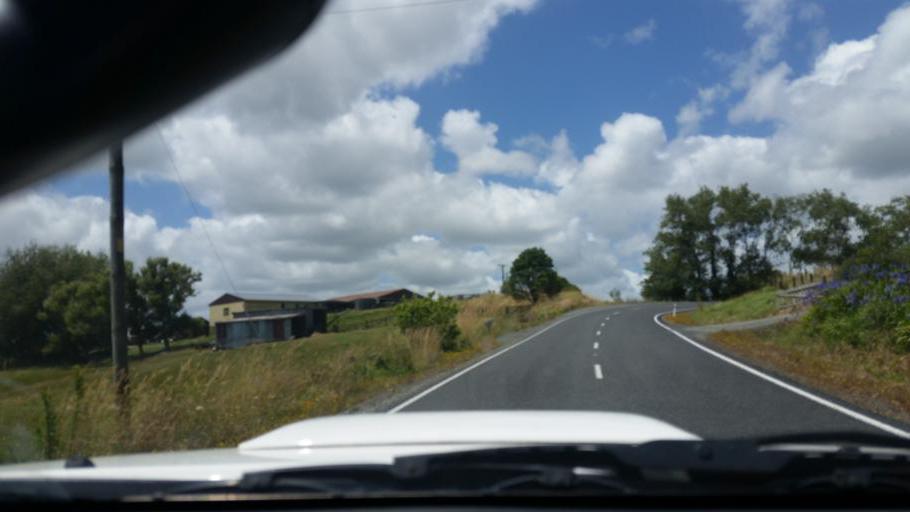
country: NZ
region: Northland
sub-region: Whangarei
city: Ruakaka
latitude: -36.0775
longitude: 174.2440
